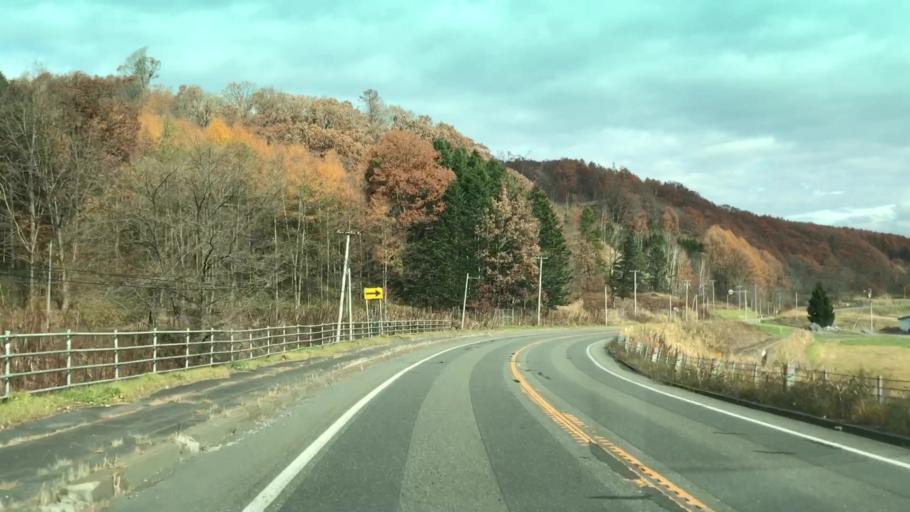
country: JP
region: Hokkaido
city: Shizunai-furukawacho
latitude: 42.7188
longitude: 142.2667
